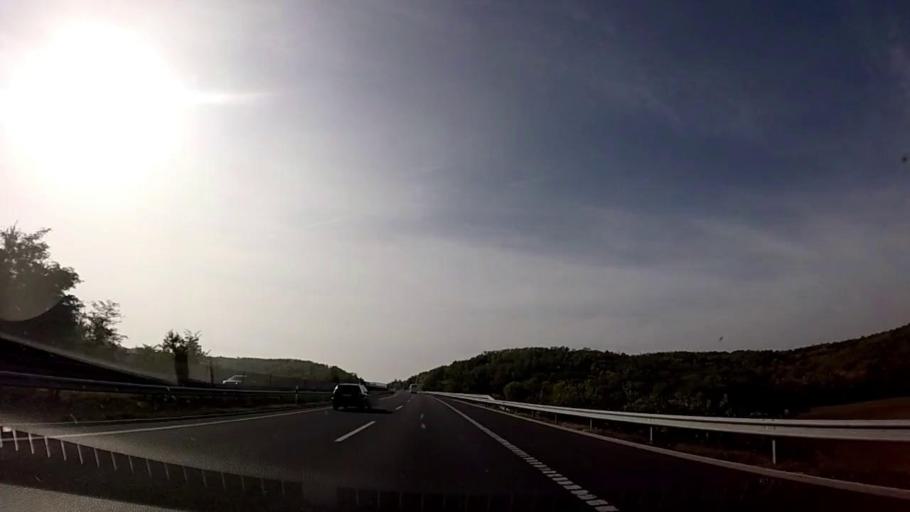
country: HU
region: Somogy
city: Zamardi
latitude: 46.8471
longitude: 17.9541
